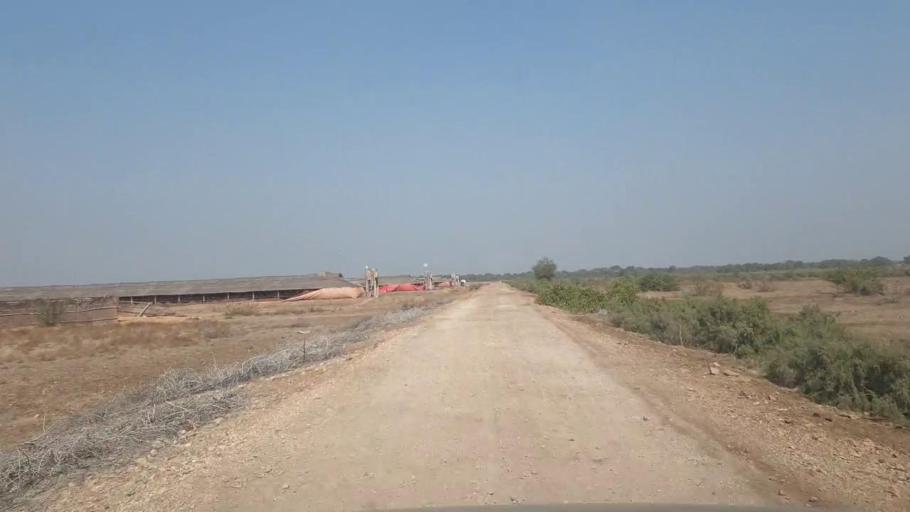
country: PK
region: Sindh
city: Tando Allahyar
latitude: 25.4396
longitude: 68.8359
